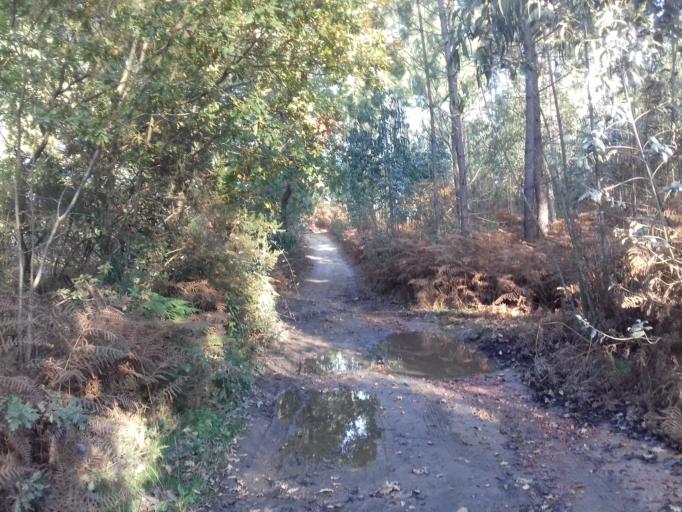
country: PT
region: Aveiro
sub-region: Albergaria-A-Velha
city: Branca
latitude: 40.7800
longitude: -8.4741
